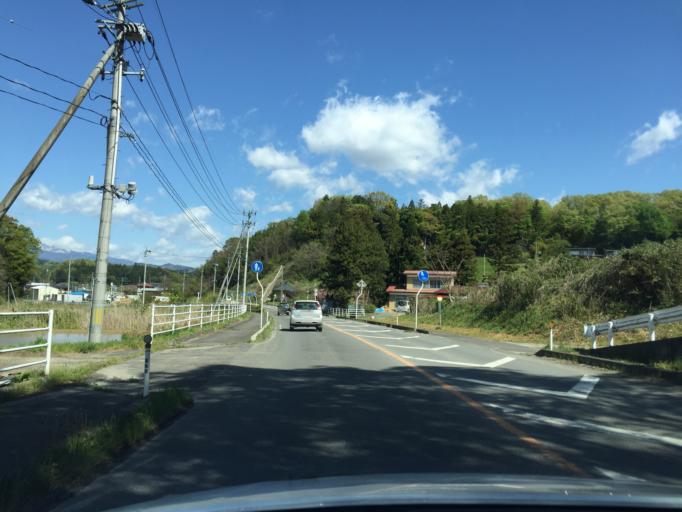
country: JP
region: Fukushima
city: Nihommatsu
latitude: 37.5796
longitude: 140.4582
